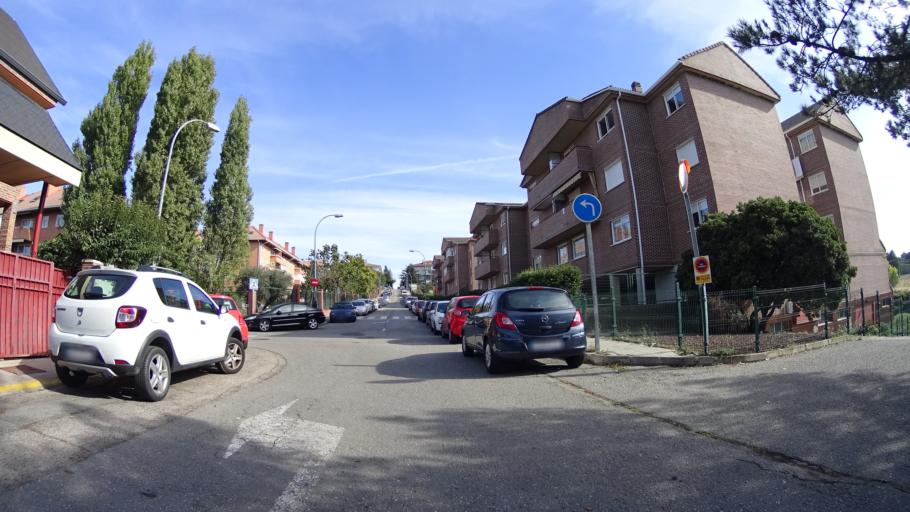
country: ES
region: Madrid
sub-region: Provincia de Madrid
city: Collado-Villalba
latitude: 40.6184
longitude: -4.0163
